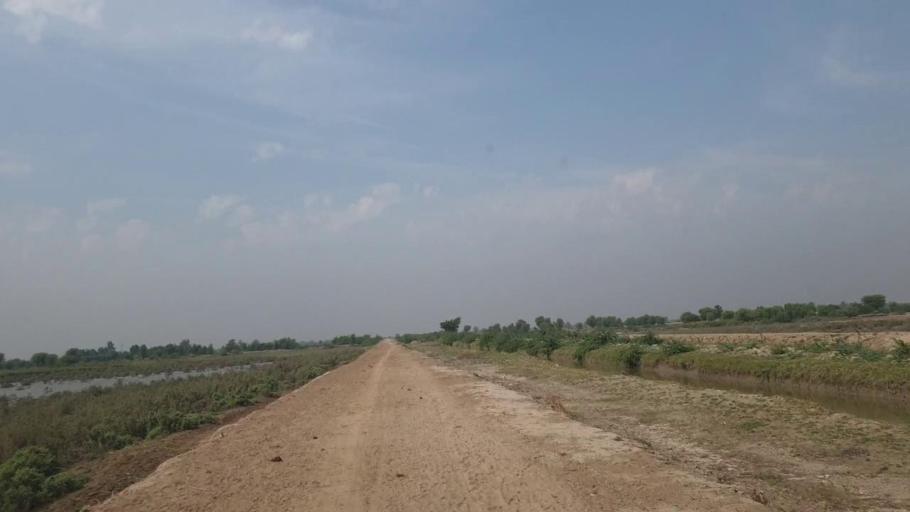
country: PK
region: Sindh
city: Rajo Khanani
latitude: 24.9592
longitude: 69.0245
